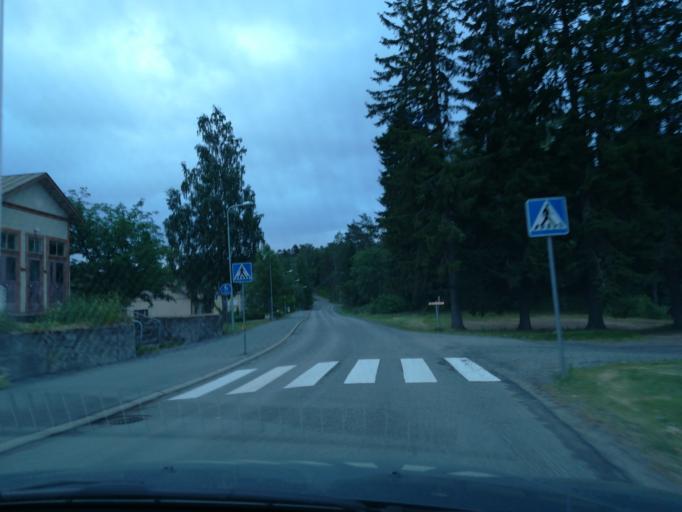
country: FI
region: Southern Savonia
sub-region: Mikkeli
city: Ristiina
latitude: 61.4997
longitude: 27.2681
